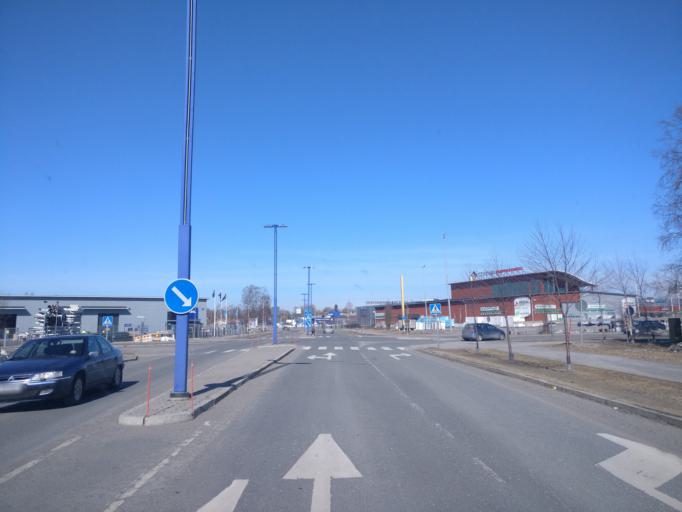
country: FI
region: Lapland
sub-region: Kemi-Tornio
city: Kemi
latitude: 65.7406
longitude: 24.5770
